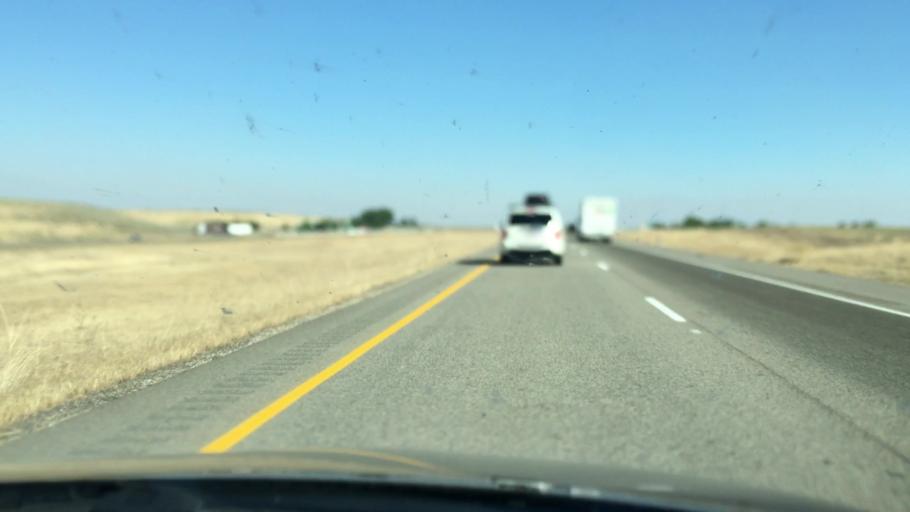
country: US
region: Idaho
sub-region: Ada County
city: Boise
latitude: 43.4818
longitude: -116.1127
